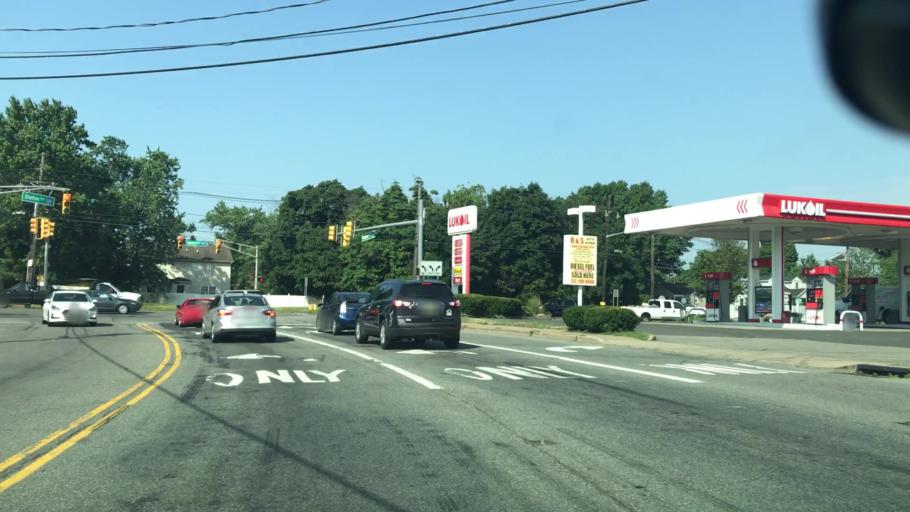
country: US
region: New Jersey
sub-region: Middlesex County
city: Society Hill
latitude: 40.5585
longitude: -74.4372
